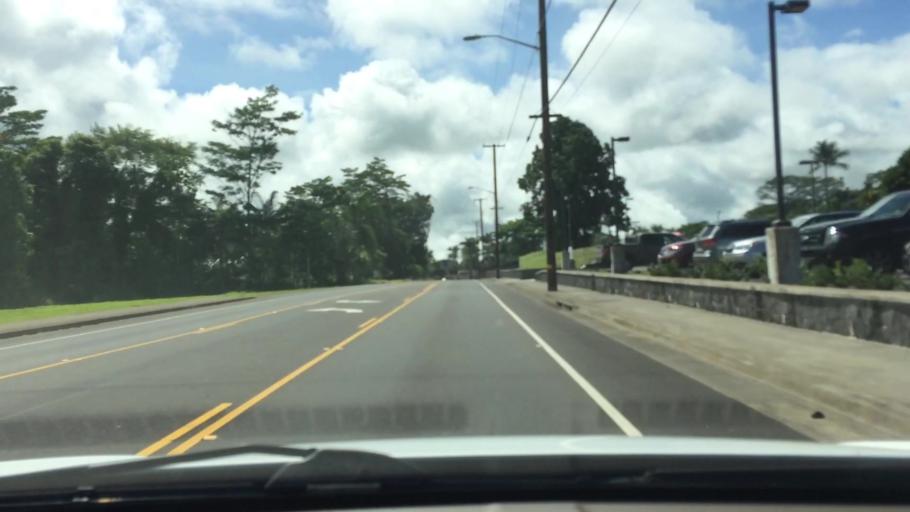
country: US
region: Hawaii
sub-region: Hawaii County
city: Hilo
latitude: 19.7034
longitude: -155.0788
